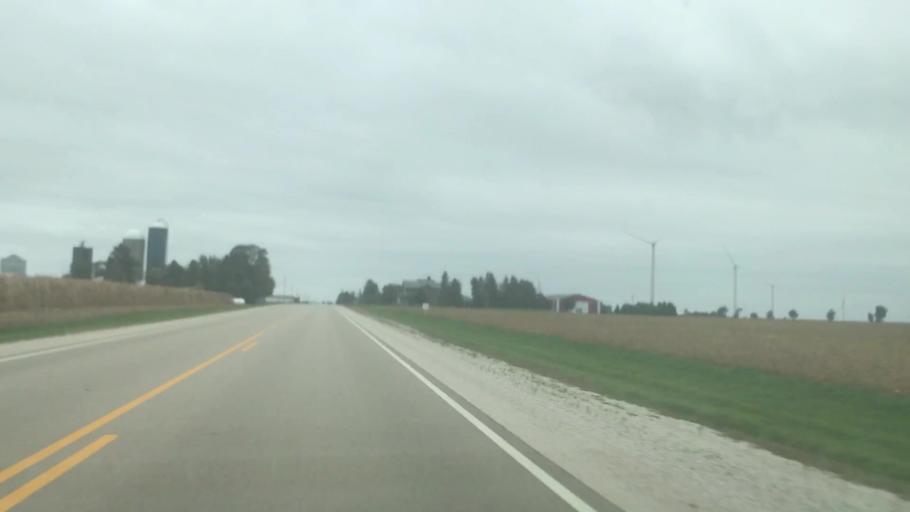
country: US
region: Wisconsin
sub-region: Fond du Lac County
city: Oakfield
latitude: 43.6292
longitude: -88.5417
